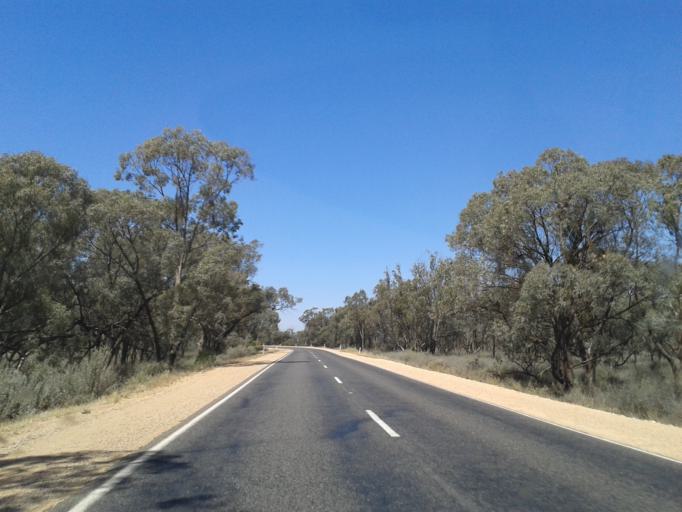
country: AU
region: Victoria
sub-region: Swan Hill
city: Swan Hill
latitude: -34.7193
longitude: 143.1130
